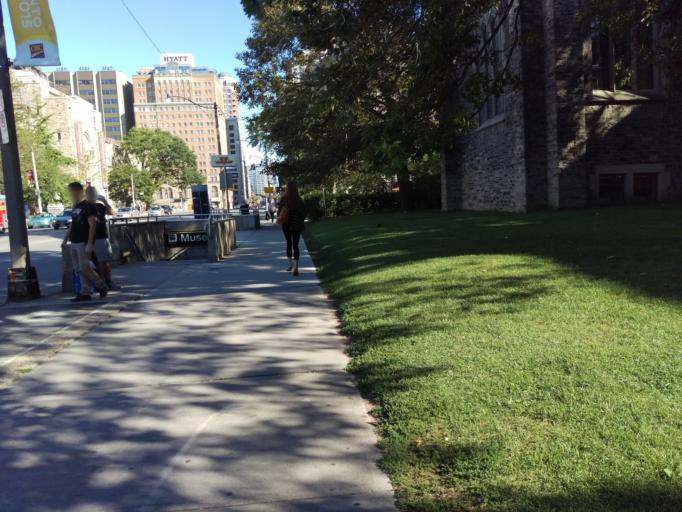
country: CA
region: Ontario
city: Toronto
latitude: 43.6669
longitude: -79.3932
